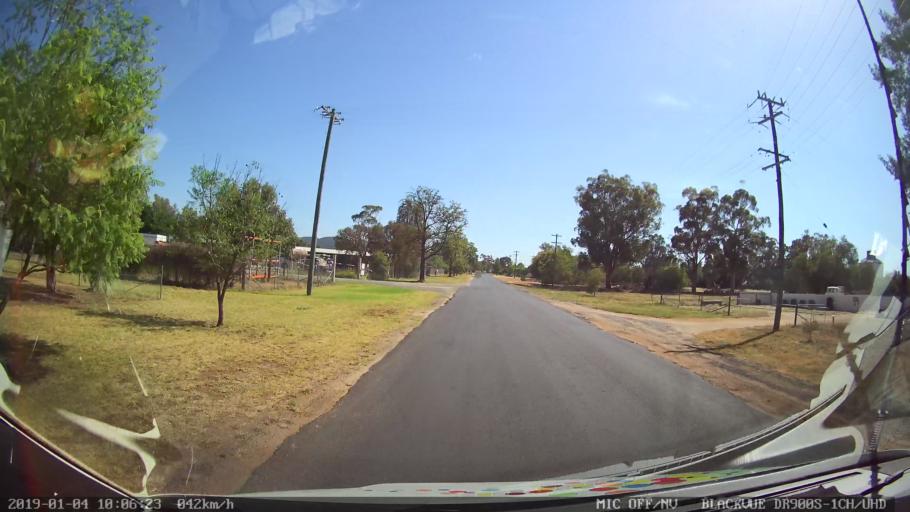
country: AU
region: New South Wales
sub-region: Cabonne
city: Canowindra
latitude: -33.4341
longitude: 148.3683
